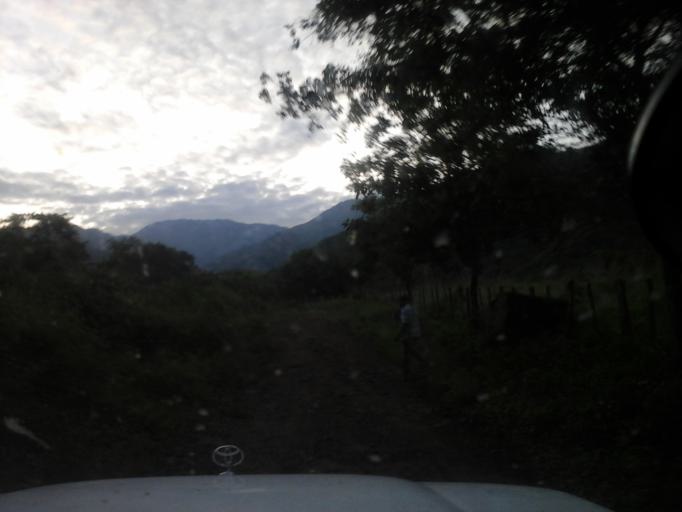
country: CO
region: Cesar
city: Agustin Codazzi
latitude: 10.1712
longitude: -73.1609
